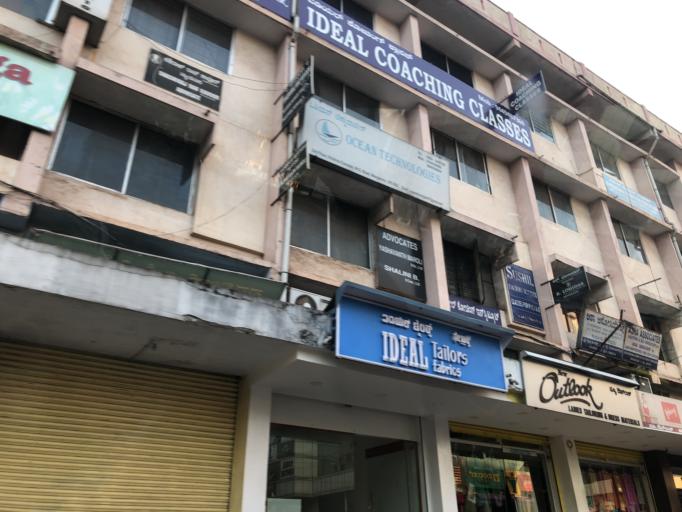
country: IN
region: Karnataka
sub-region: Dakshina Kannada
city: Mangalore
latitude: 12.8767
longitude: 74.8417
